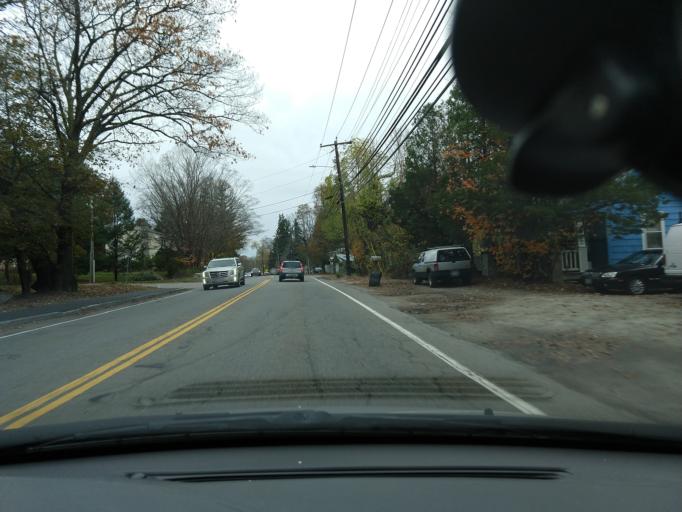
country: US
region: Massachusetts
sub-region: Middlesex County
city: Chelmsford
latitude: 42.6117
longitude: -71.3586
